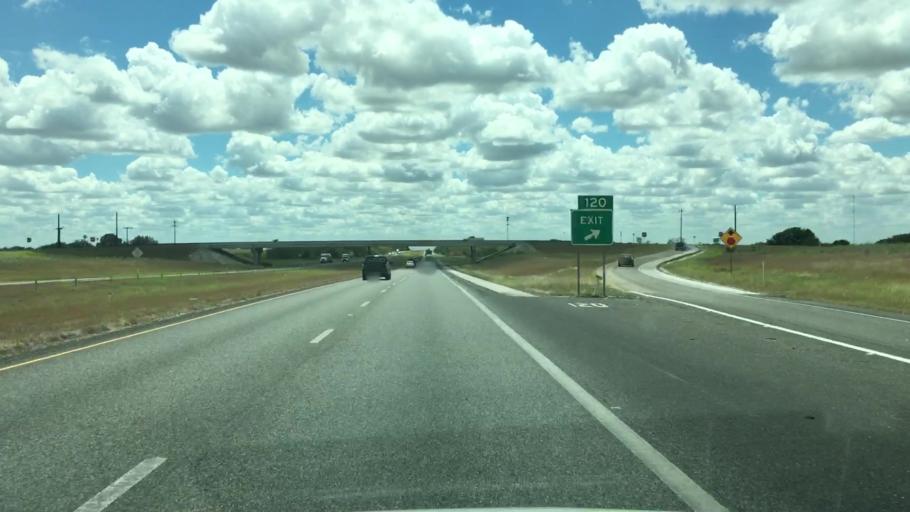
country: US
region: Texas
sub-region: Bexar County
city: Elmendorf
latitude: 29.1438
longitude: -98.4287
